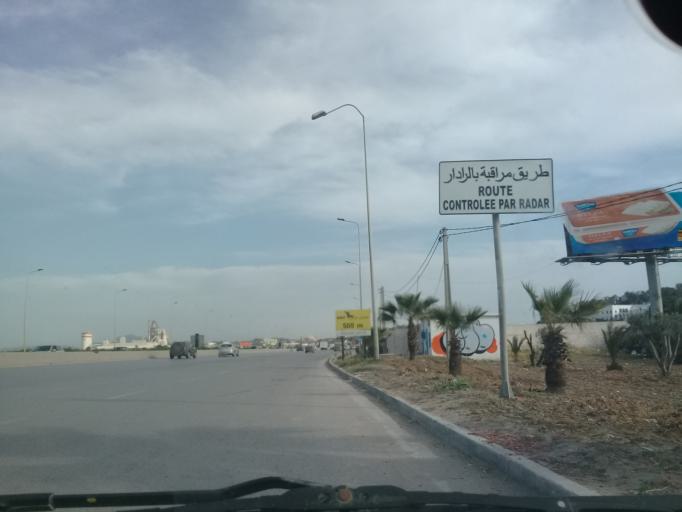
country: TN
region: Tunis
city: Tunis
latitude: 36.7913
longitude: 10.1910
